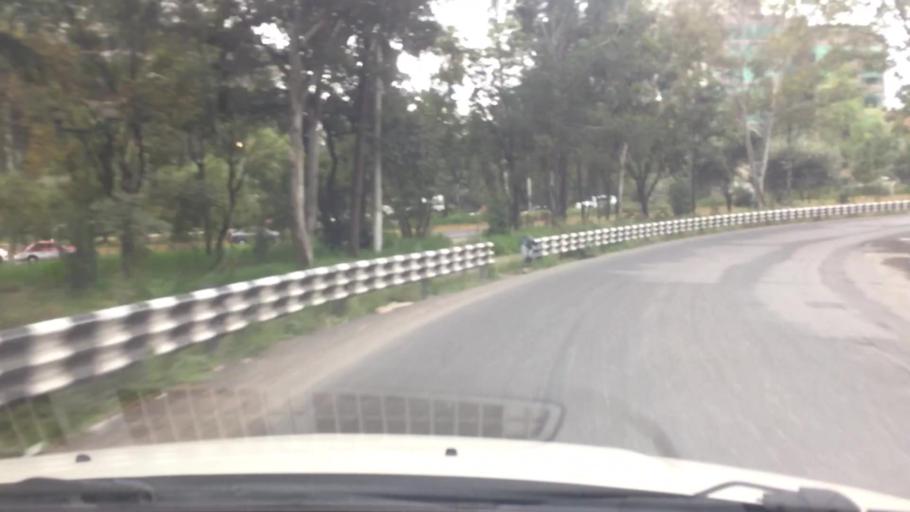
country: MX
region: Mexico City
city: Magdalena Contreras
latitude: 19.3042
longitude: -99.2068
